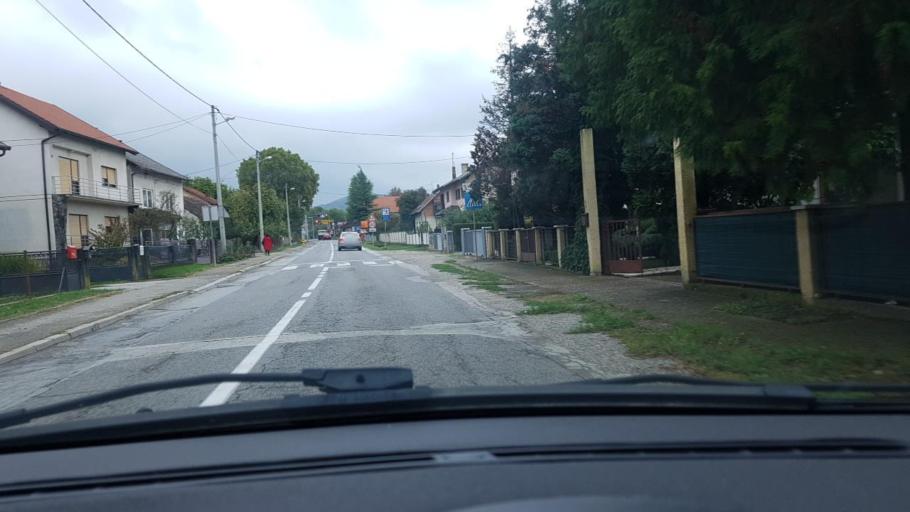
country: HR
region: Grad Zagreb
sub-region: Sesvete
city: Sesvete
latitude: 45.9045
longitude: 16.1258
